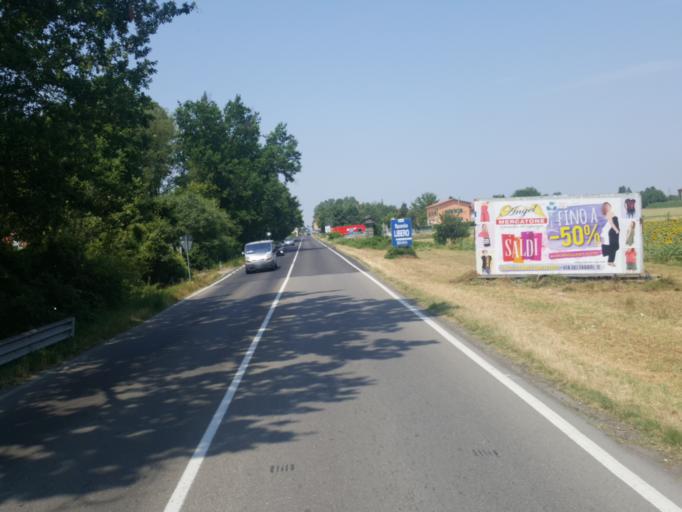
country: IT
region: Emilia-Romagna
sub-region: Provincia di Bologna
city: Calcara
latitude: 44.5611
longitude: 11.1498
